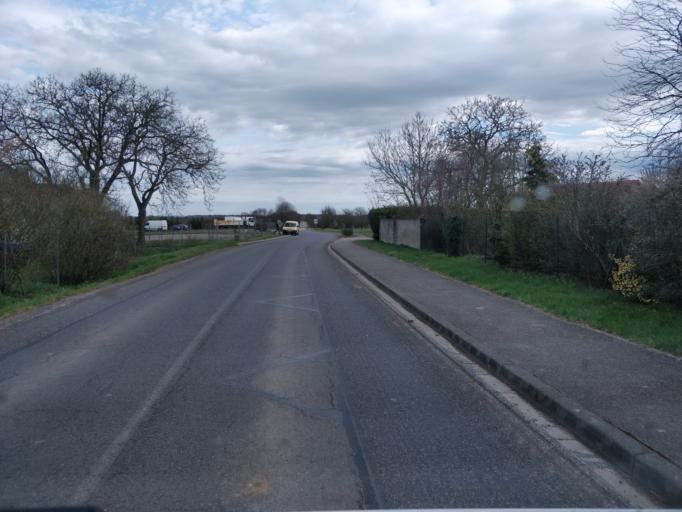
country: FR
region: Lorraine
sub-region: Departement de Meurthe-et-Moselle
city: Jarny
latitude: 49.0767
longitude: 5.8854
